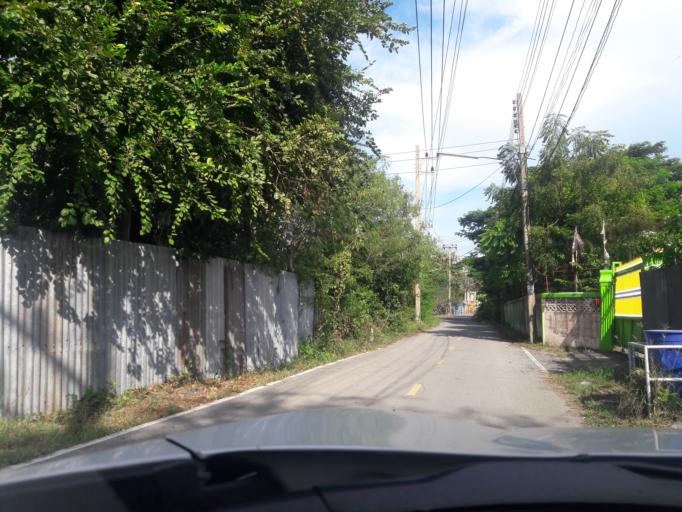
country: TH
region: Lop Buri
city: Ban Mi
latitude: 15.0503
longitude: 100.5408
